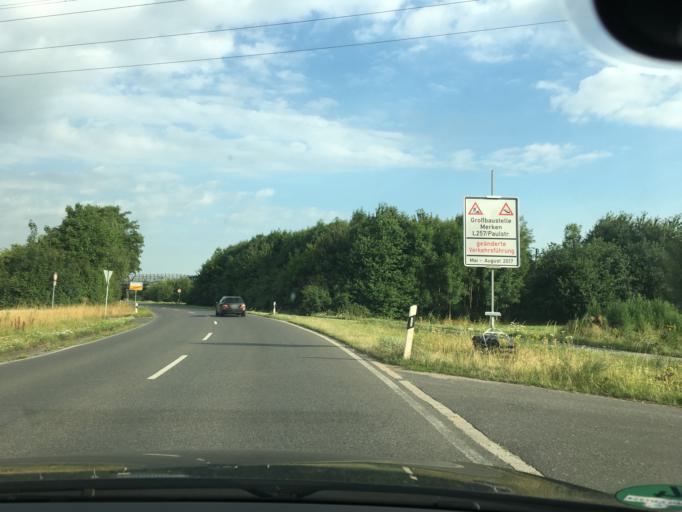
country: DE
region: North Rhine-Westphalia
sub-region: Regierungsbezirk Koln
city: Niederzier
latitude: 50.8340
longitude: 6.4407
